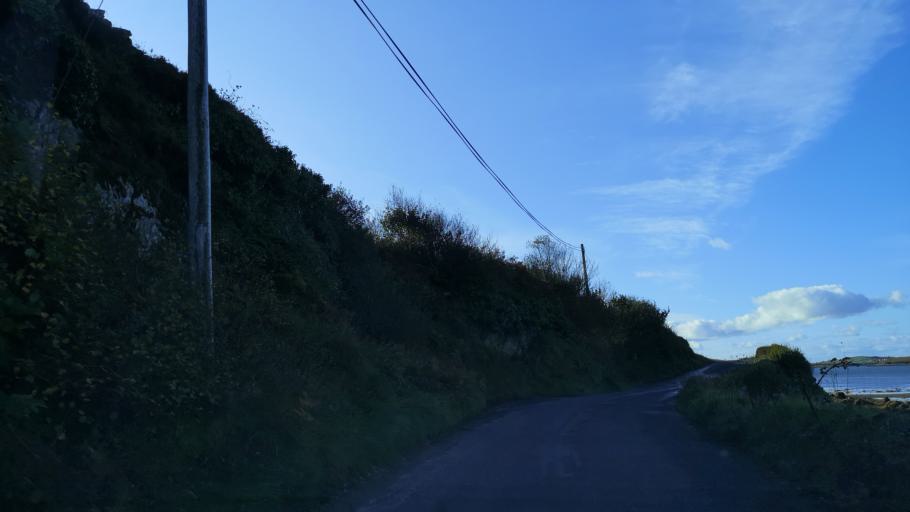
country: IE
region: Connaught
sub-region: County Galway
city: Clifden
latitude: 53.5054
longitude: -10.0480
